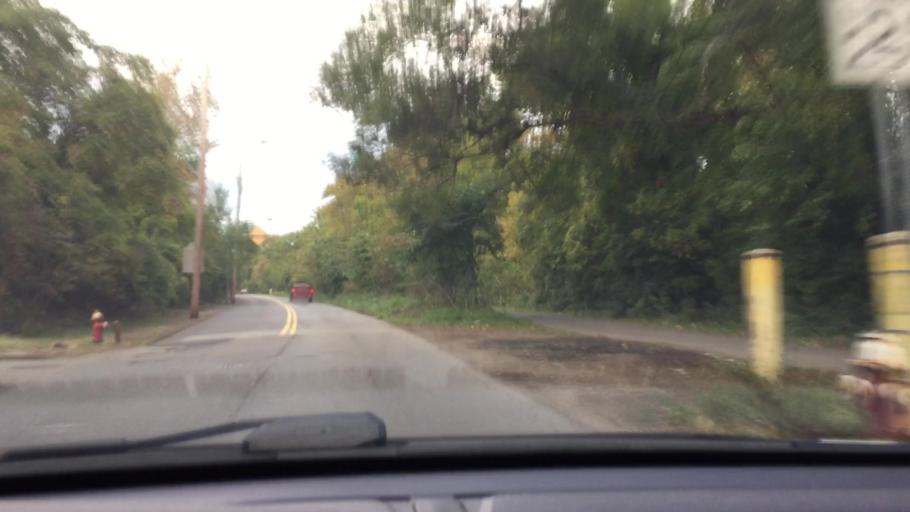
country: US
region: Pennsylvania
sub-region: Allegheny County
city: Millvale
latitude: 40.4604
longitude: -79.9823
